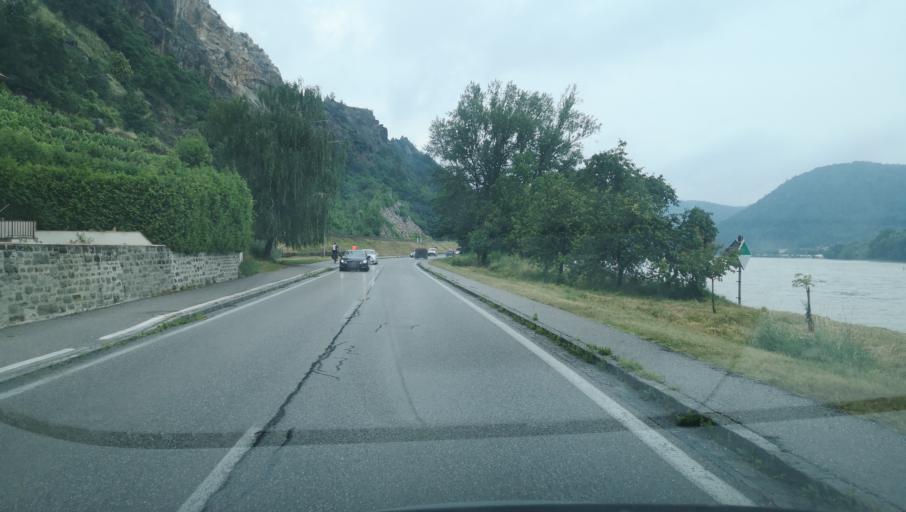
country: AT
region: Lower Austria
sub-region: Politischer Bezirk Krems
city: Durnstein
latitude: 48.4032
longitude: 15.5157
